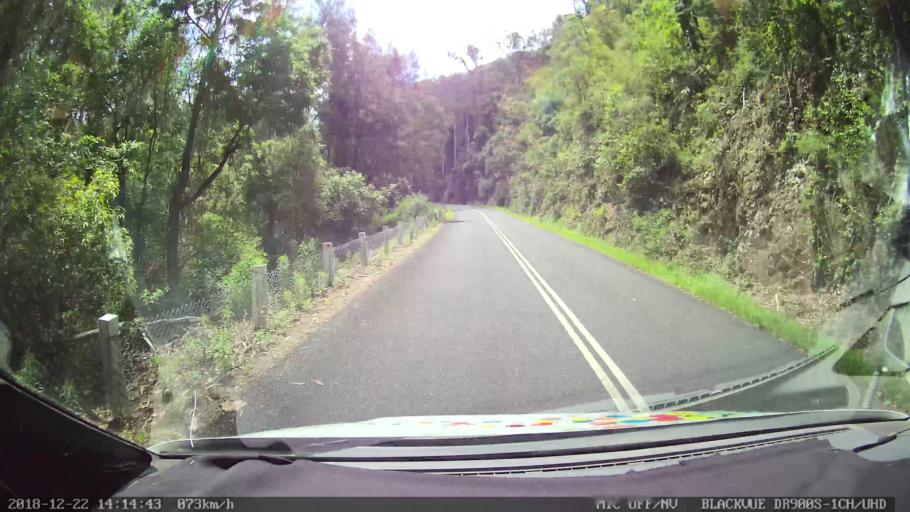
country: AU
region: New South Wales
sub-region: Clarence Valley
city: Coutts Crossing
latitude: -29.9987
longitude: 152.6845
